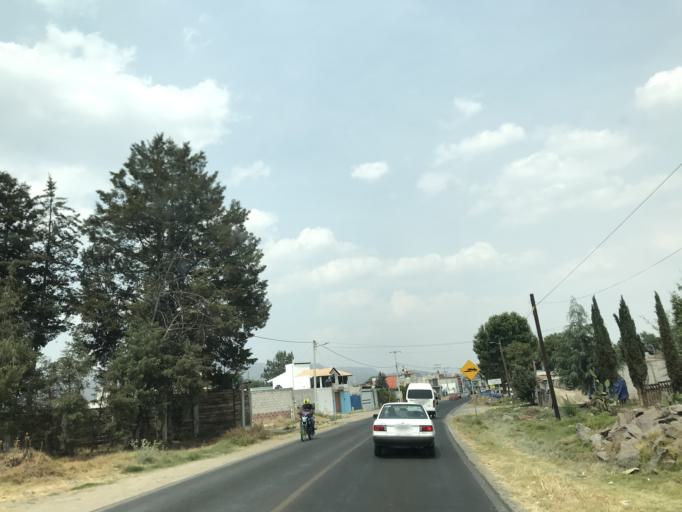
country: MX
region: Tlaxcala
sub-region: Ixtacuixtla de Mariano Matamoros
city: Santa Justina Ecatepec
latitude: 19.3175
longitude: -98.3187
